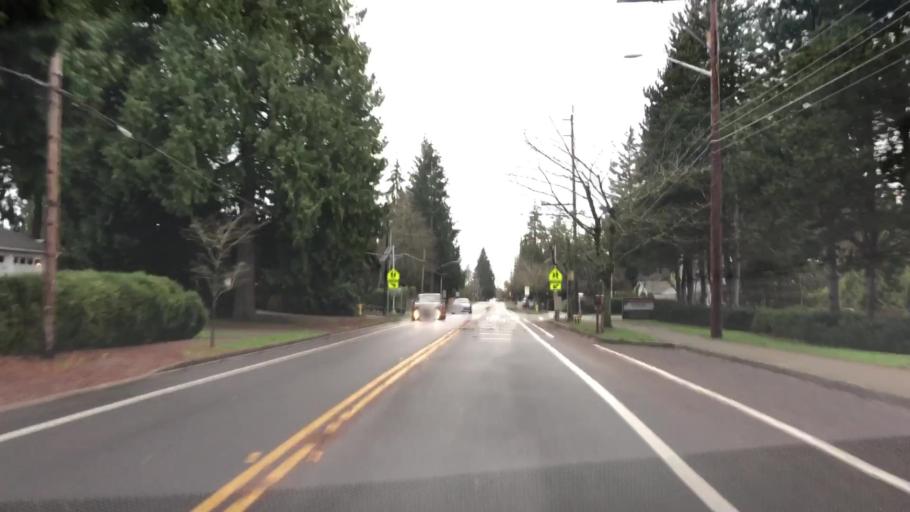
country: US
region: Washington
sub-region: King County
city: Kirkland
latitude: 47.6753
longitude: -122.1685
